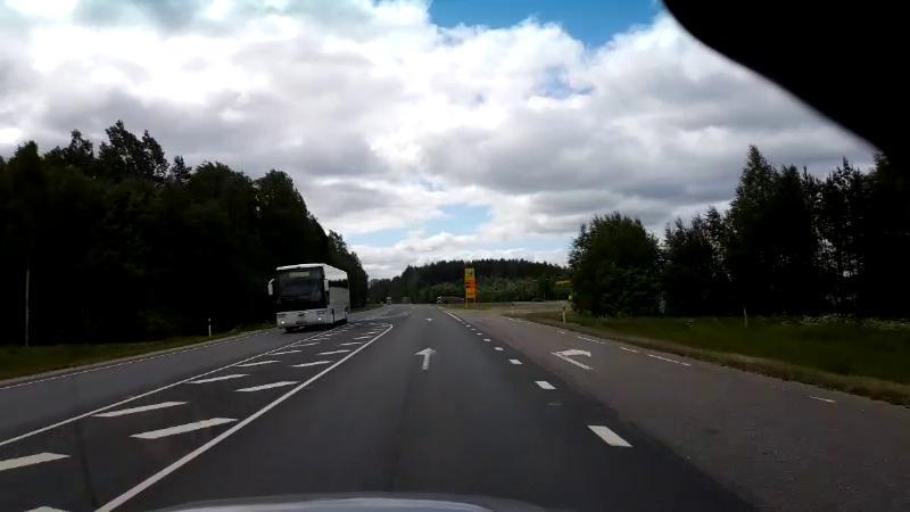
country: EE
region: Paernumaa
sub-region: Halinga vald
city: Parnu-Jaagupi
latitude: 58.7036
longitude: 24.4258
